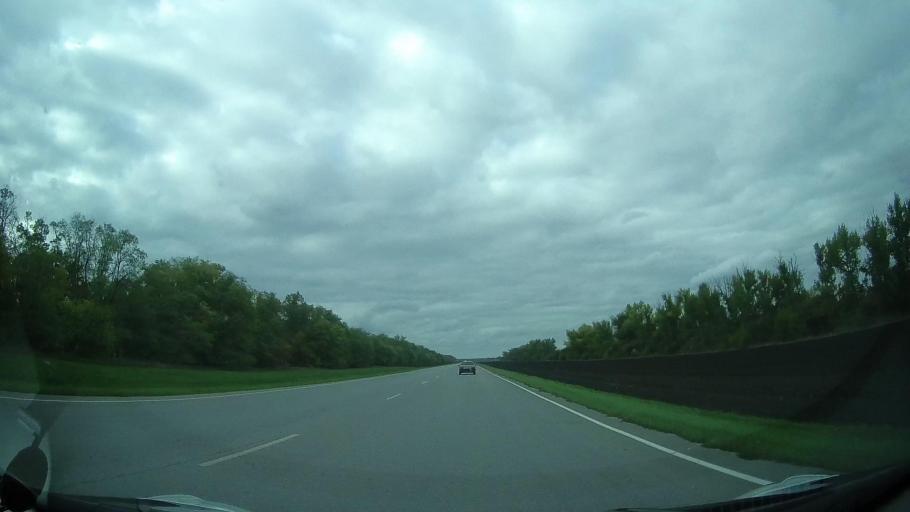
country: RU
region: Rostov
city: Yegorlykskaya
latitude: 46.6381
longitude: 40.5814
